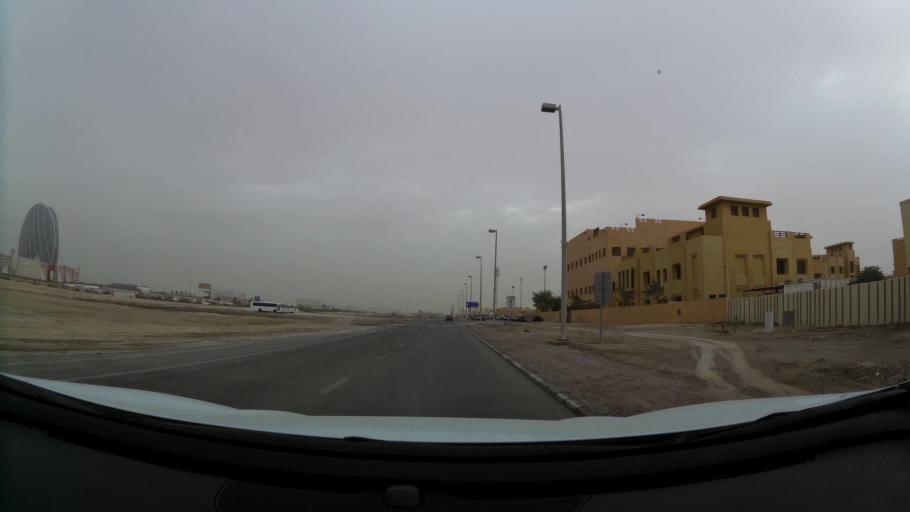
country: AE
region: Abu Dhabi
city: Abu Dhabi
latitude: 24.4352
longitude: 54.5733
